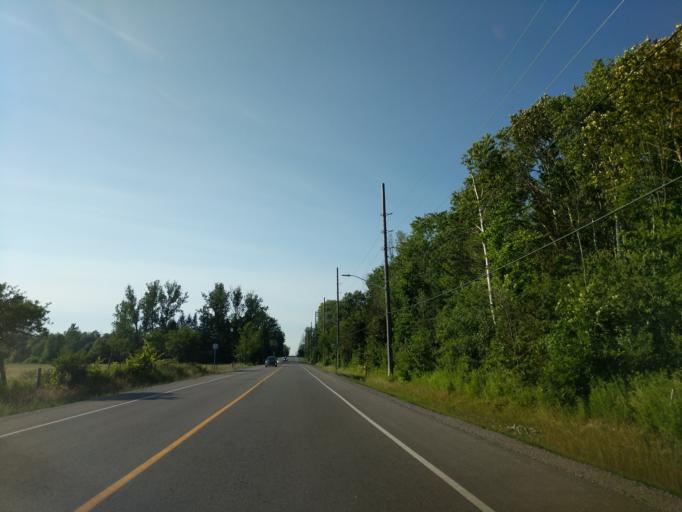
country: CA
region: Ontario
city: Oshawa
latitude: 43.9329
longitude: -78.9110
